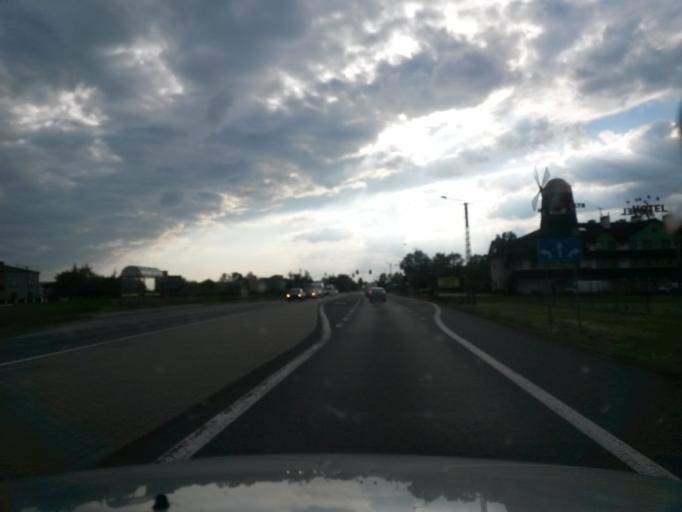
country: PL
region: Lodz Voivodeship
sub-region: Powiat piotrkowski
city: Wola Krzysztoporska
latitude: 51.4146
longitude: 19.5864
